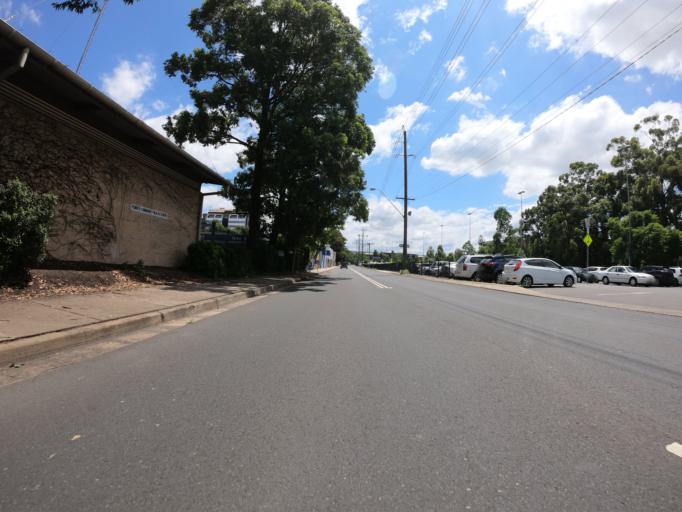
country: AU
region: New South Wales
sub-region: Penrith Municipality
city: Penrith
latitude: -33.7517
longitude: 150.6996
